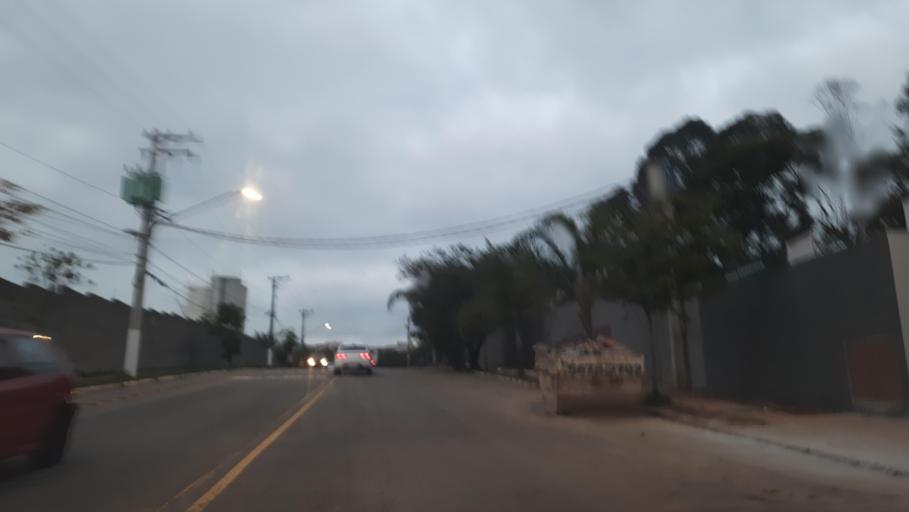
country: BR
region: Sao Paulo
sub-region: Caieiras
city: Caieiras
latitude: -23.4448
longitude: -46.7262
